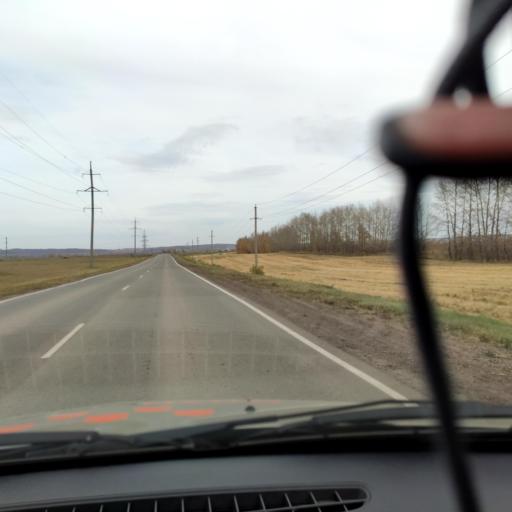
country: RU
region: Bashkortostan
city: Kabakovo
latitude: 54.5325
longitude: 56.0686
